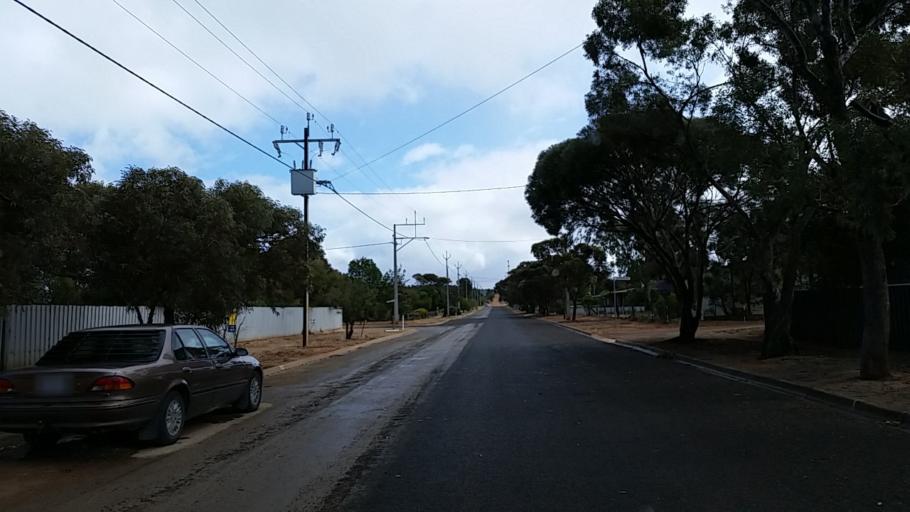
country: AU
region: South Australia
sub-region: Peterborough
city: Peterborough
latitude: -32.9696
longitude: 138.8317
